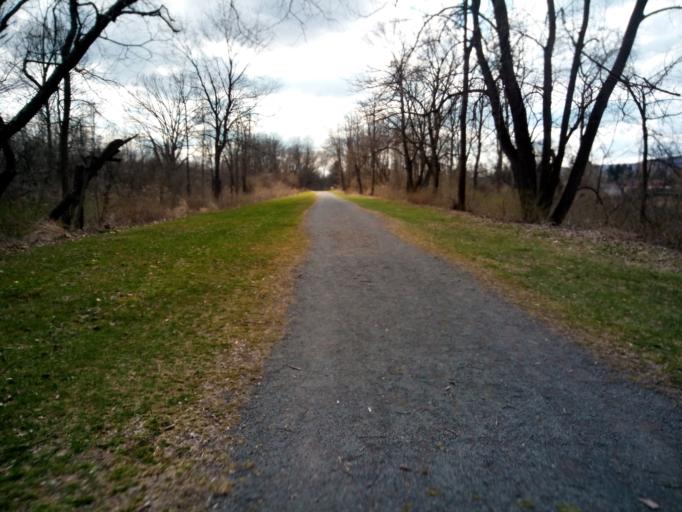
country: US
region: New York
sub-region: Chemung County
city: Big Flats
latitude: 42.1417
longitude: -76.9238
